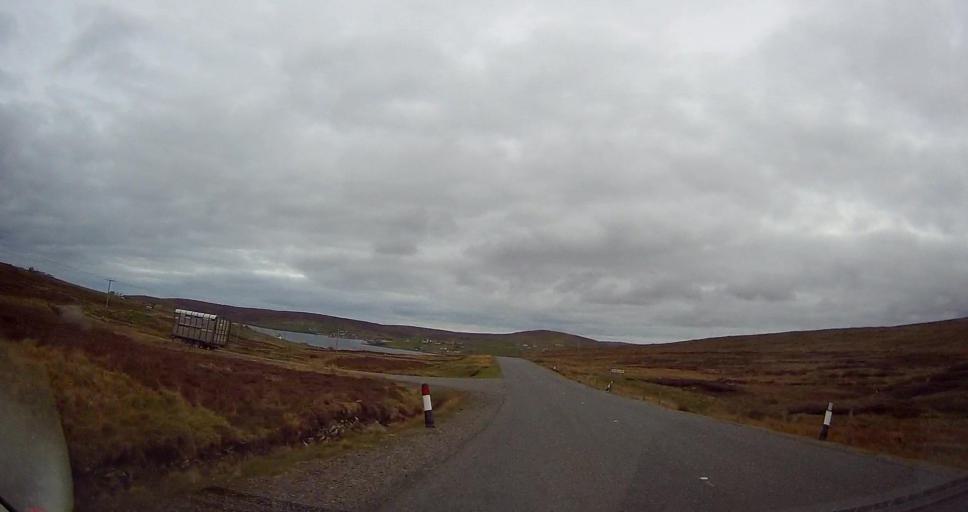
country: GB
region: Scotland
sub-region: Shetland Islands
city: Shetland
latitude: 60.6201
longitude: -1.0748
